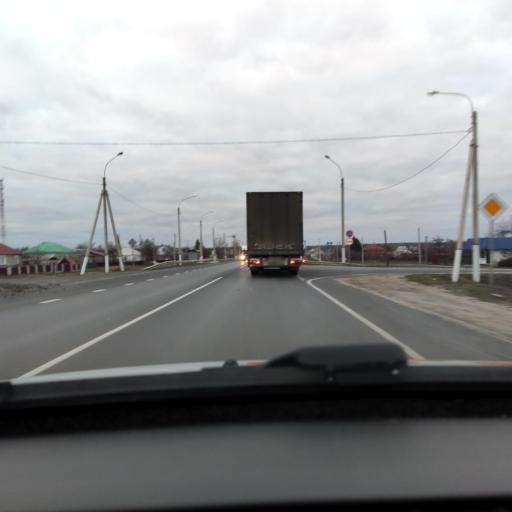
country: RU
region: Lipetsk
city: Khlevnoye
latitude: 52.2544
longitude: 39.1517
